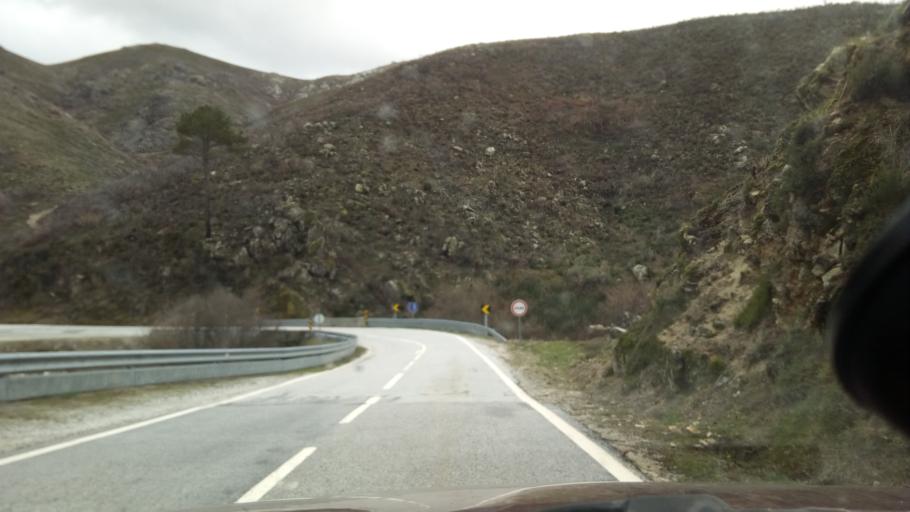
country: PT
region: Guarda
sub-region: Manteigas
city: Manteigas
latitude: 40.4504
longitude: -7.5873
